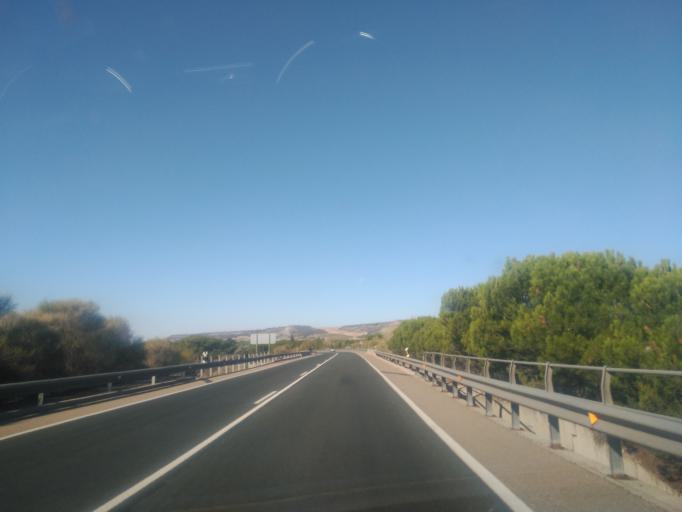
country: ES
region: Castille and Leon
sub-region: Provincia de Valladolid
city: Quintanilla de Onesimo
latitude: 41.6210
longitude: -4.3759
